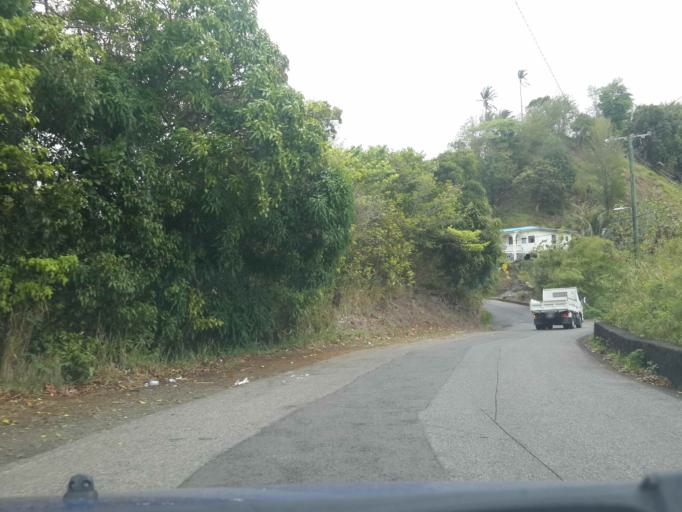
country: LC
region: Castries Quarter
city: Castries
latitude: 13.9938
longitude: -60.9778
